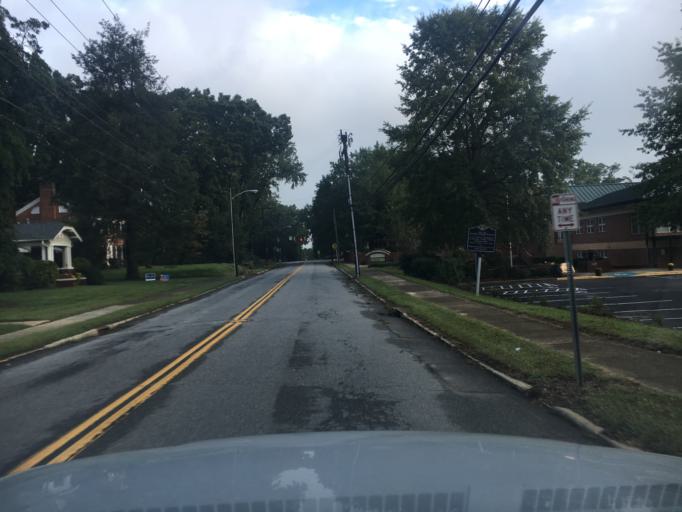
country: US
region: North Carolina
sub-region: Catawba County
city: Hickory
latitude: 35.7366
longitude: -81.3444
